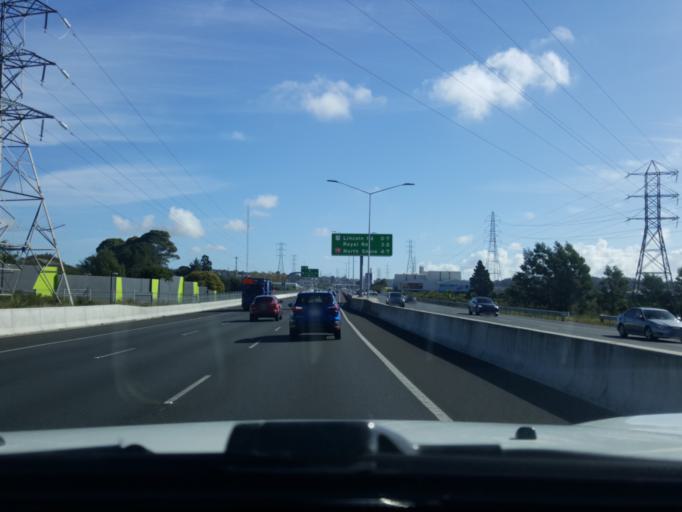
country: NZ
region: Auckland
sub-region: Auckland
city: Rosebank
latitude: -36.8541
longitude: 174.6429
